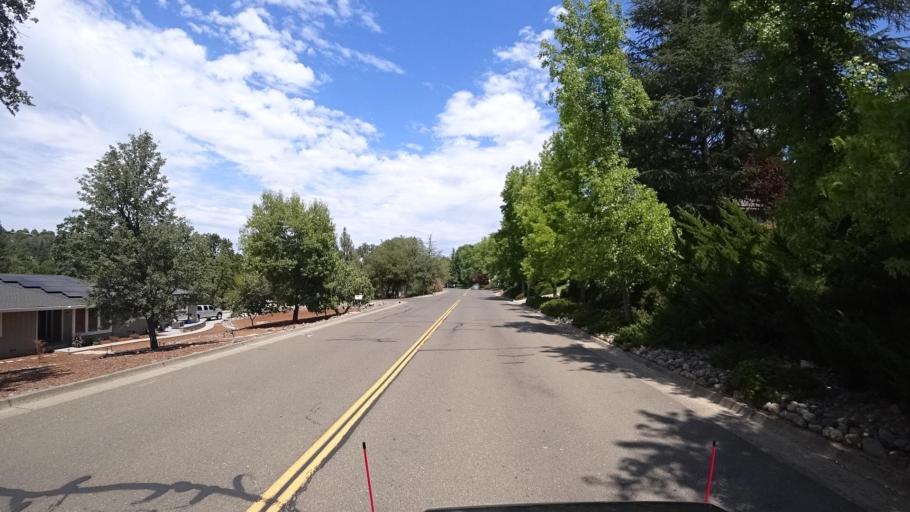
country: US
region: California
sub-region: Placer County
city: Rocklin
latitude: 38.8115
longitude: -121.2355
